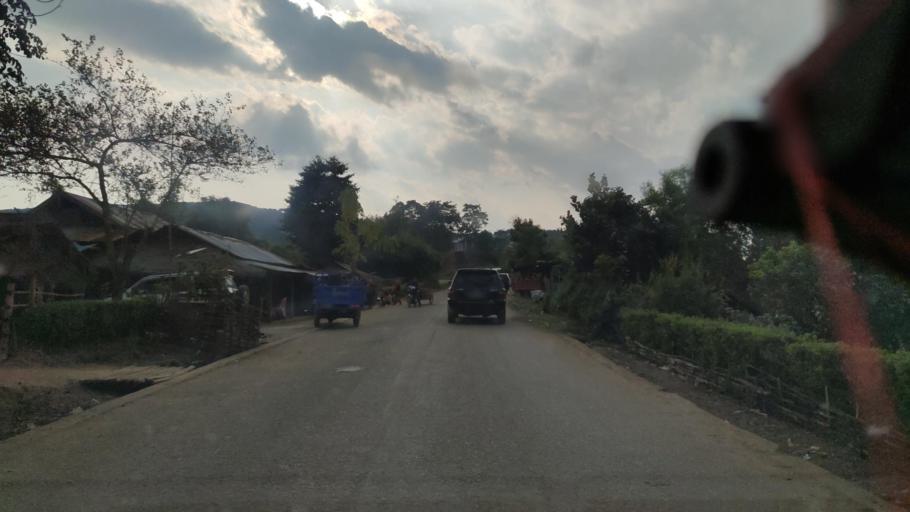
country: CN
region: Yunnan
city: Menghai
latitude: 21.4485
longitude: 99.6986
